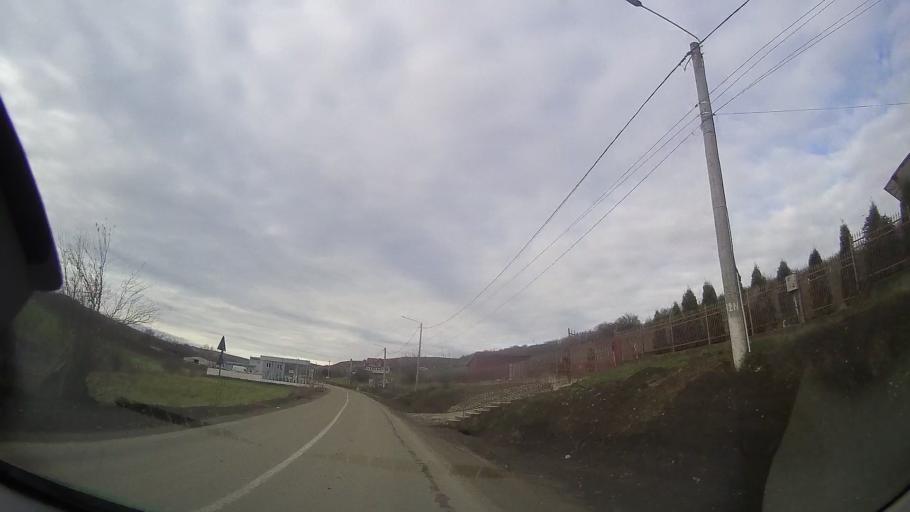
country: RO
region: Bistrita-Nasaud
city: Frunzi
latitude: 46.8977
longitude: 24.3359
